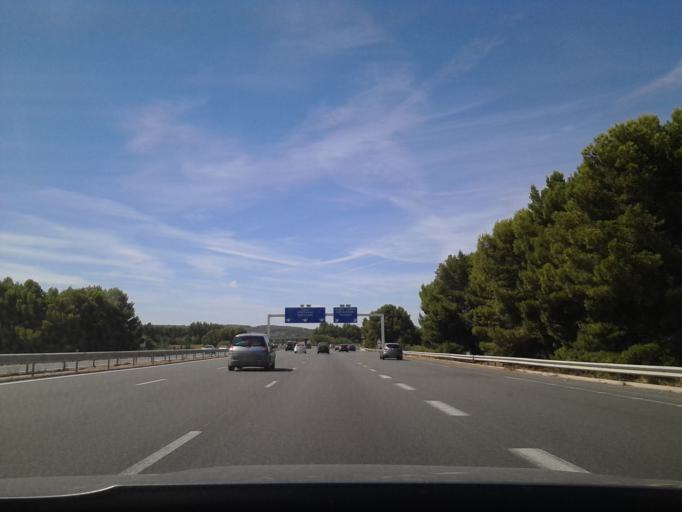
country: FR
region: Languedoc-Roussillon
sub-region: Departement de l'Aude
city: Narbonne
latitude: 43.1551
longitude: 2.9860
